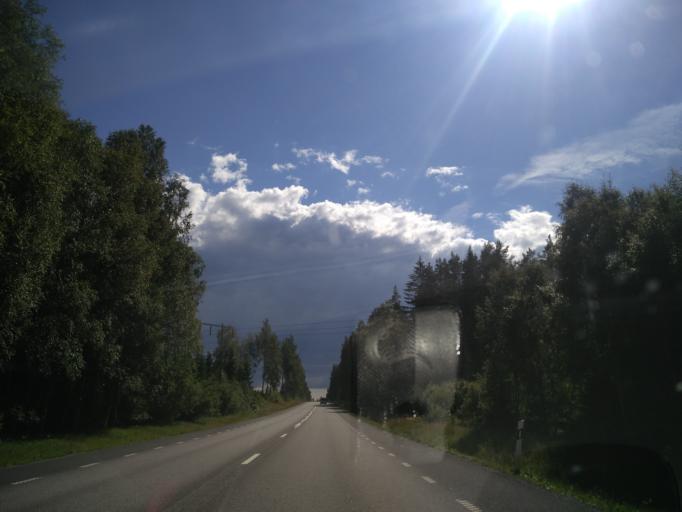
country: SE
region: OErebro
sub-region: Hallefors Kommun
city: Haellefors
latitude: 59.7597
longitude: 14.5152
